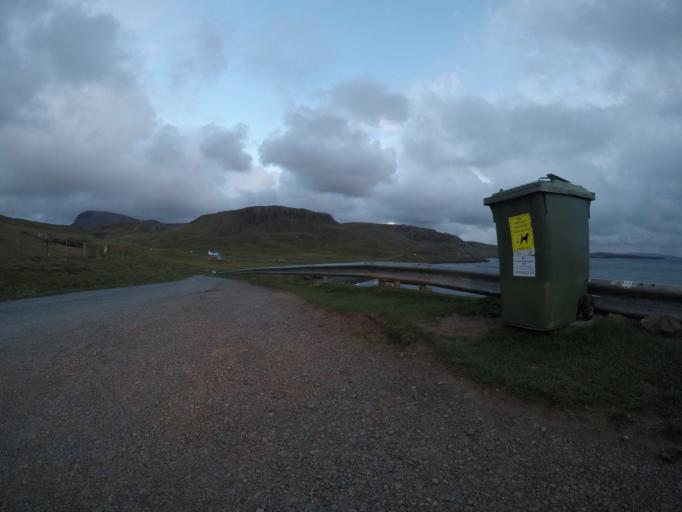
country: GB
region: Scotland
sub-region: Highland
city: Portree
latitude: 57.6816
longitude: -6.3453
